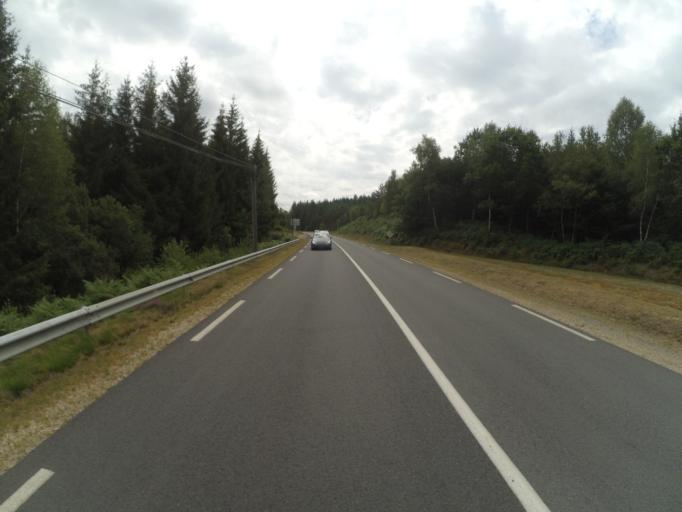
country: FR
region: Limousin
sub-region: Departement de la Creuse
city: La Courtine
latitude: 45.6496
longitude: 2.2668
